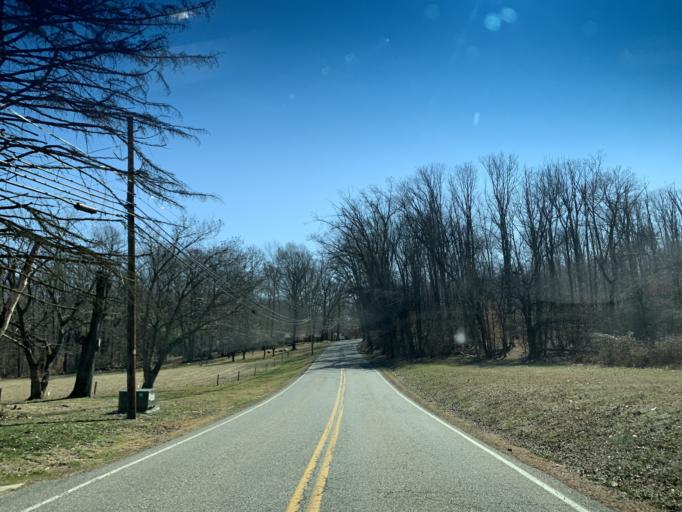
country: US
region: Maryland
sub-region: Cecil County
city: Perryville
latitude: 39.6122
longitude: -76.0740
